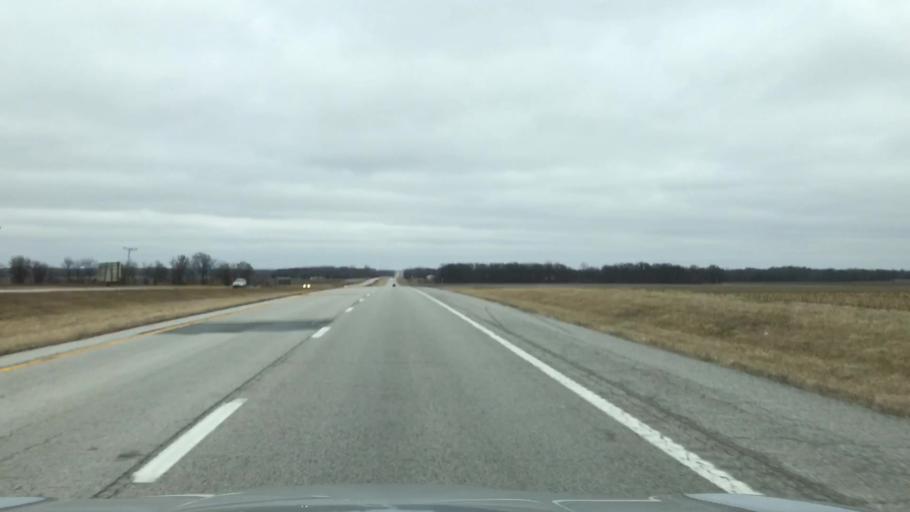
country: US
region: Missouri
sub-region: Livingston County
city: Chillicothe
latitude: 39.7764
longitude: -93.4594
